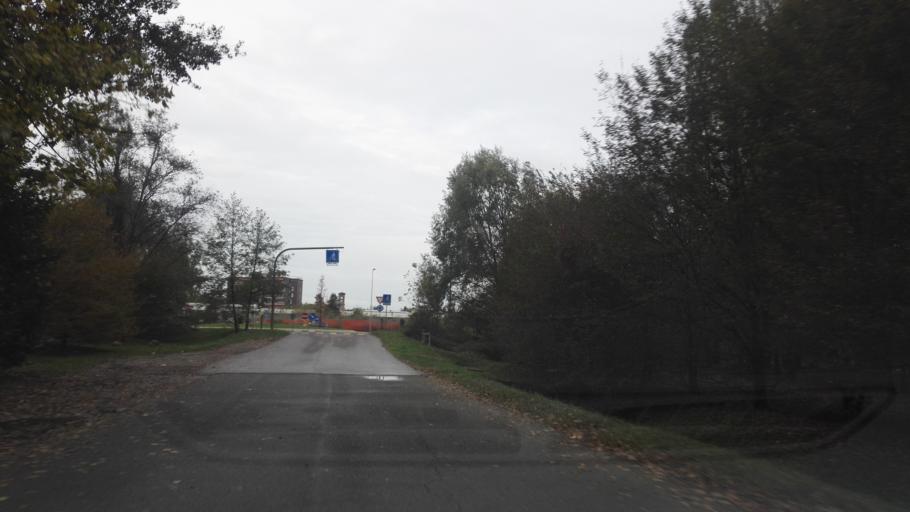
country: IT
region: Lombardy
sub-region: Citta metropolitana di Milano
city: Bettola-Zeloforomagno
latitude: 45.4218
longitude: 9.2978
